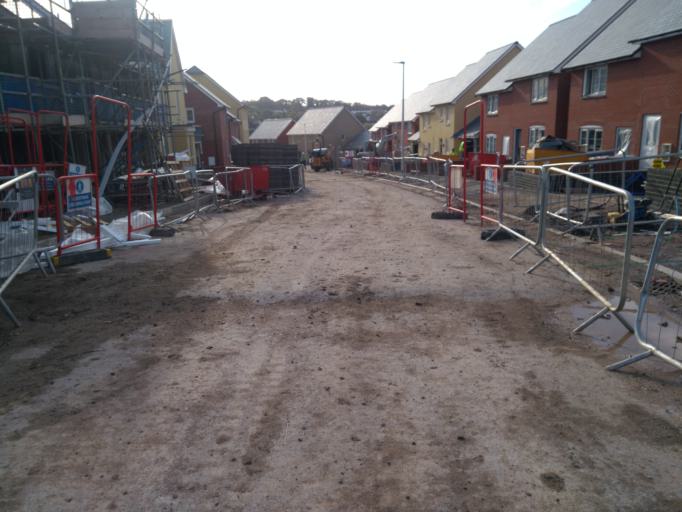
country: GB
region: England
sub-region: Devon
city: Kingsteignton
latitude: 50.5335
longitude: -3.5860
